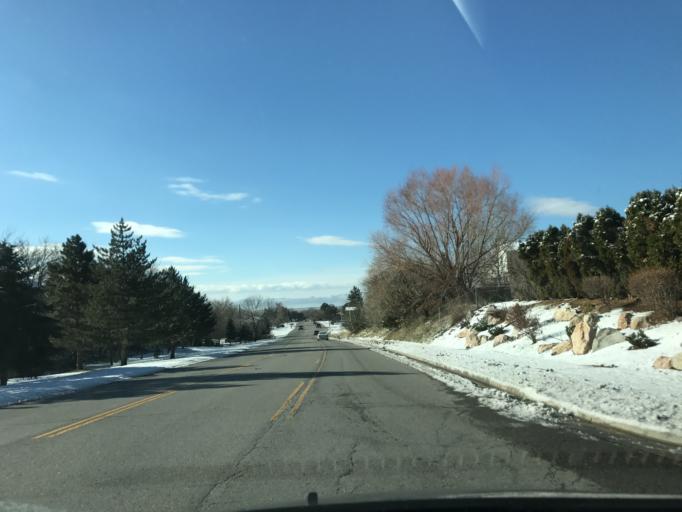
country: US
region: Utah
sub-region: Davis County
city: Fruit Heights
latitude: 41.0410
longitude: -111.9155
